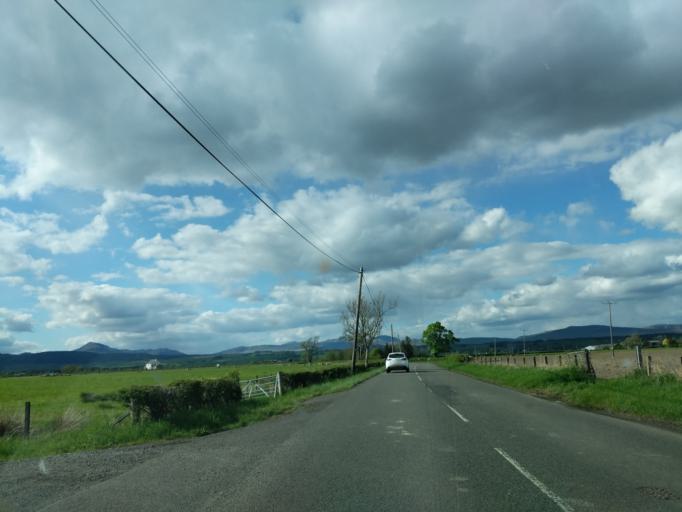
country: GB
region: Scotland
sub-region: Stirling
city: Doune
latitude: 56.1406
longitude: -4.1453
